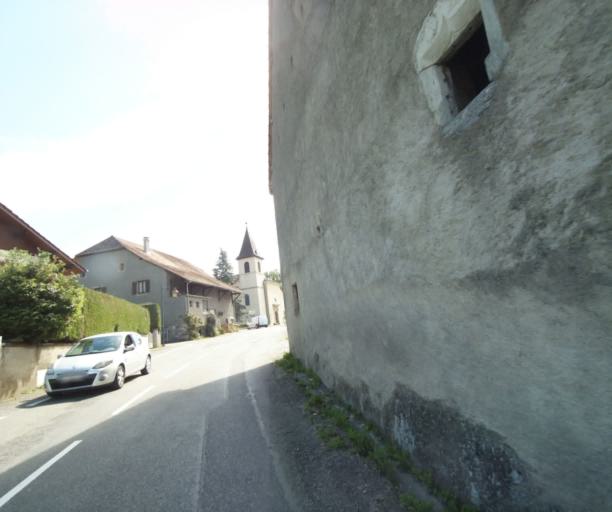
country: FR
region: Rhone-Alpes
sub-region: Departement de la Haute-Savoie
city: Perrignier
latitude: 46.2866
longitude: 6.4413
